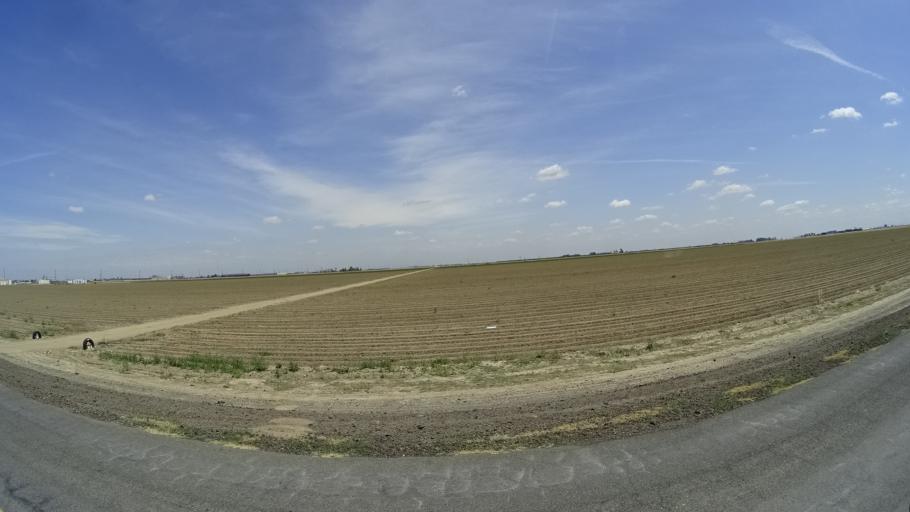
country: US
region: California
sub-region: Kings County
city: Home Garden
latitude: 36.2510
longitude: -119.6729
